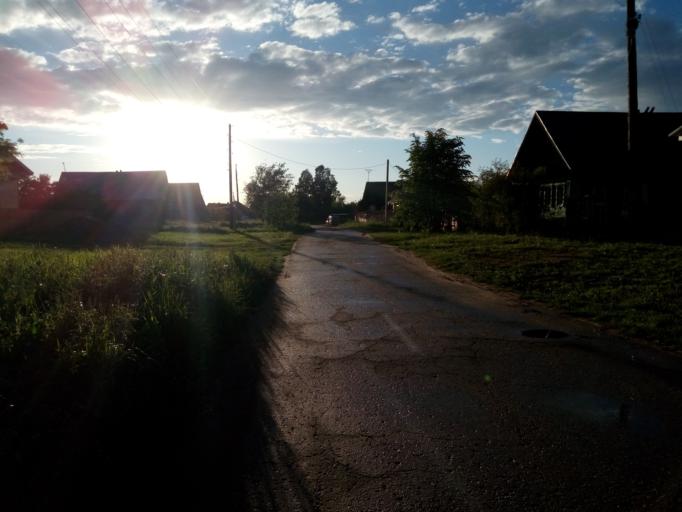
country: RU
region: Nizjnij Novgorod
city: Voskresenskoye
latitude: 56.7744
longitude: 45.5495
